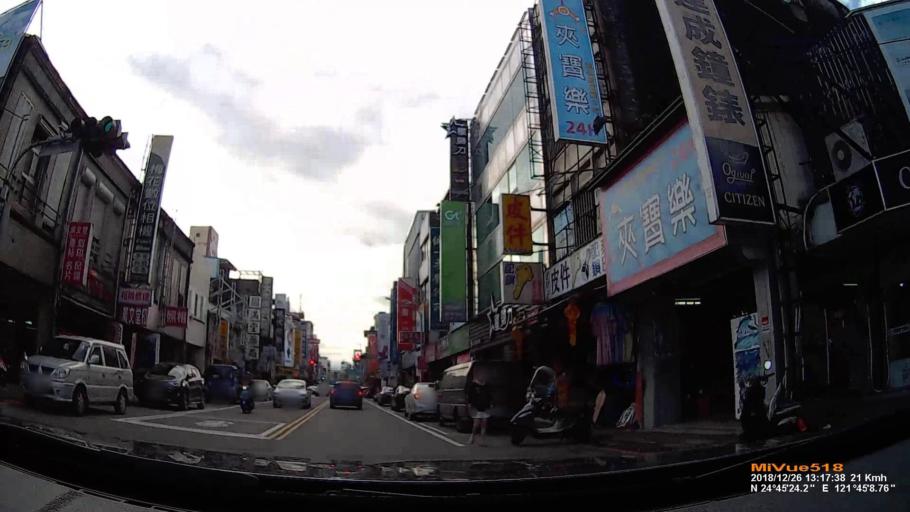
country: TW
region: Taiwan
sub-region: Yilan
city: Yilan
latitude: 24.7476
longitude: 121.7547
